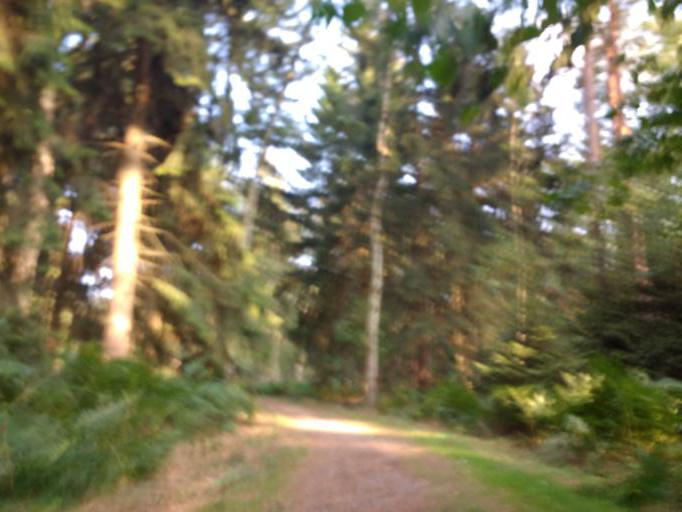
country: DE
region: Lower Saxony
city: Gifhorn
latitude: 52.4614
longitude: 10.5536
